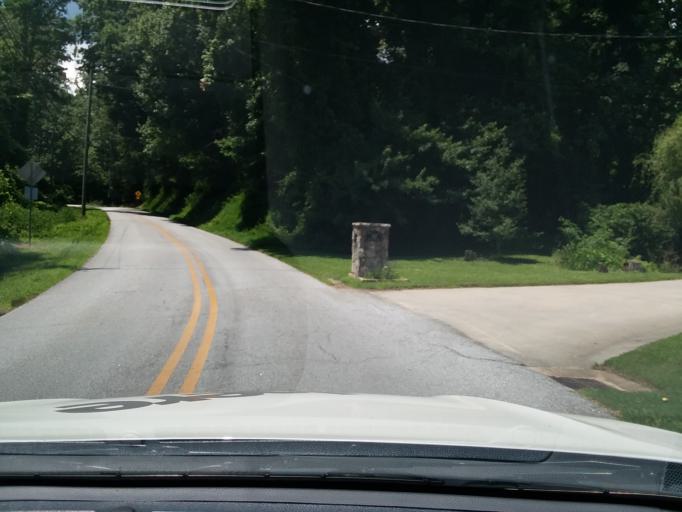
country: US
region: Georgia
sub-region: Rabun County
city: Clayton
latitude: 34.7746
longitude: -83.4302
